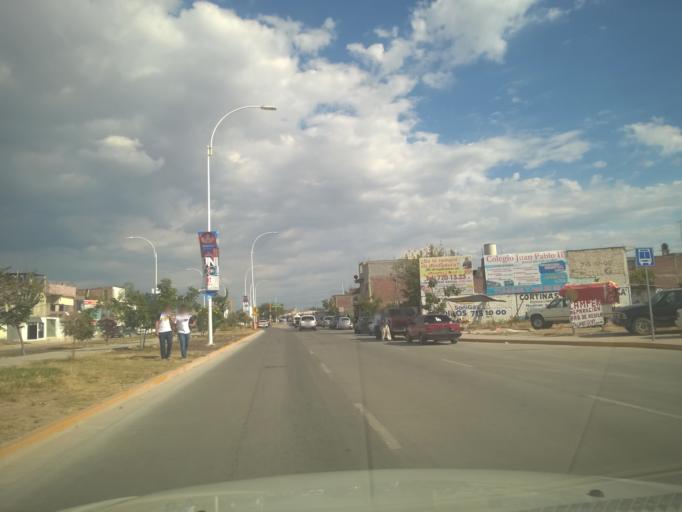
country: MX
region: Guanajuato
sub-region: Leon
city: San Jose de Duran (Los Troncoso)
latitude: 21.0636
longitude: -101.6277
